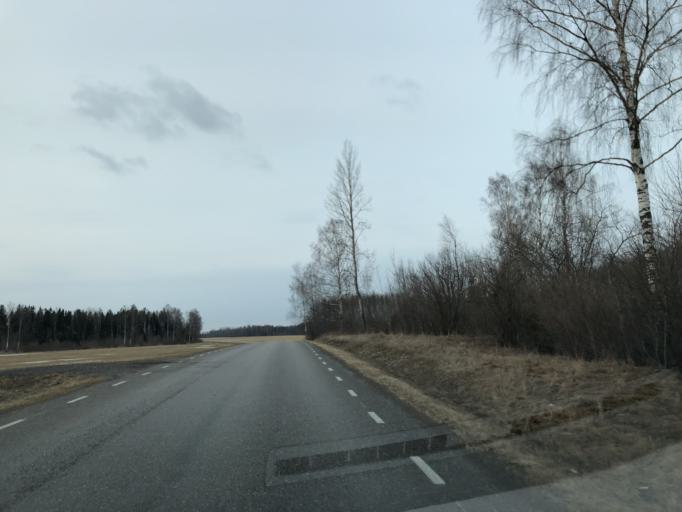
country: EE
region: Paernumaa
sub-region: Vaendra vald (alev)
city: Vandra
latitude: 58.6732
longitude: 25.0114
